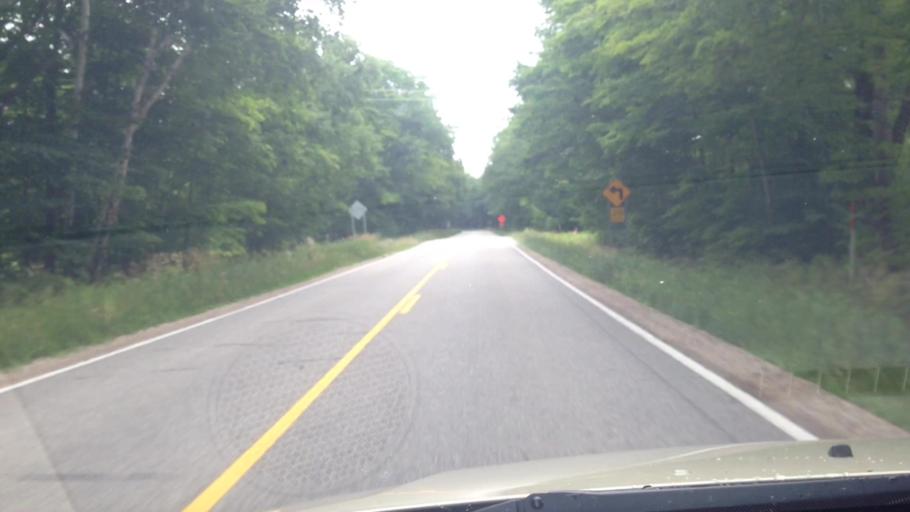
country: US
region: Michigan
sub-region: Mackinac County
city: Saint Ignace
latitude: 46.0467
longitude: -85.1097
